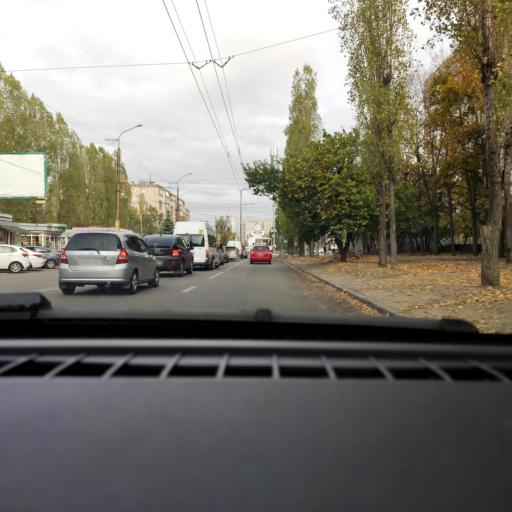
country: RU
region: Voronezj
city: Podgornoye
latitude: 51.7114
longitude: 39.1737
